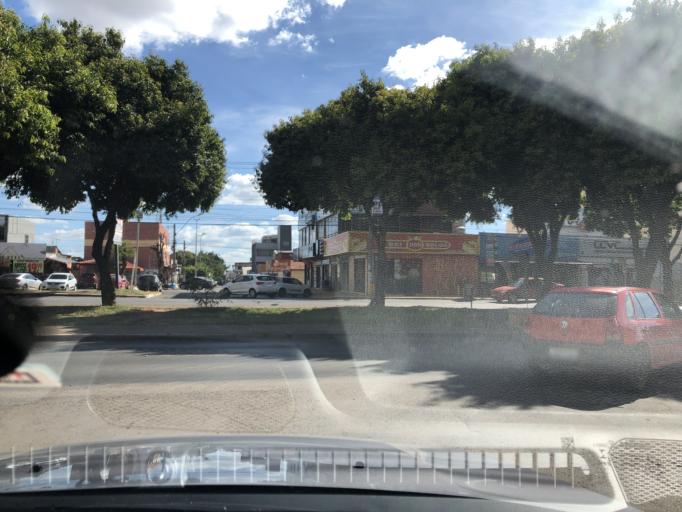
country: BR
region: Federal District
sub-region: Brasilia
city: Brasilia
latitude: -15.7961
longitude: -48.1207
